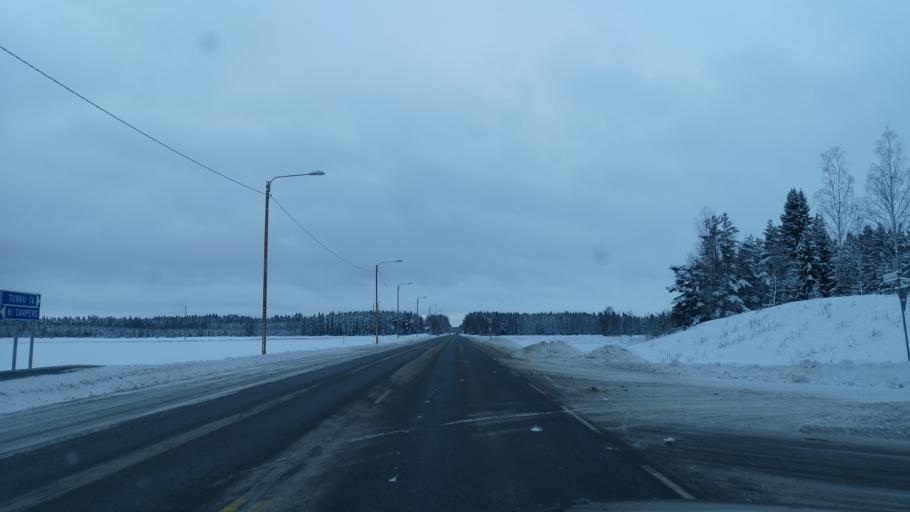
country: FI
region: Haeme
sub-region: Forssa
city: Ypaejae
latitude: 60.9184
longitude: 23.1978
